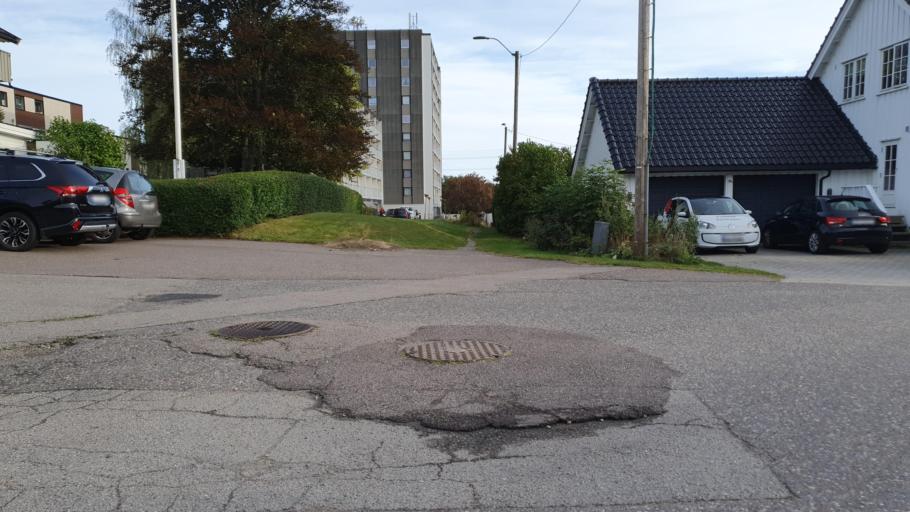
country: NO
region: Vestfold
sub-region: Tonsberg
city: Tonsberg
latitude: 59.2752
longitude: 10.4246
